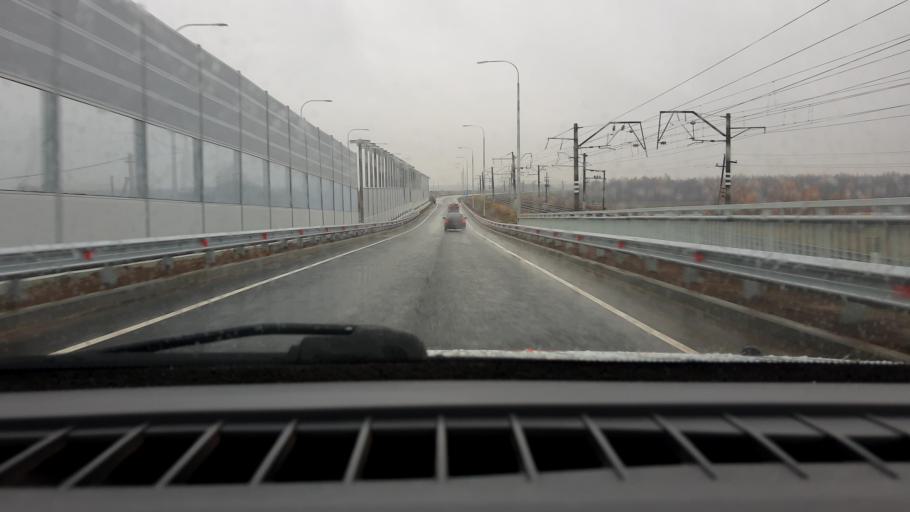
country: RU
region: Nizjnij Novgorod
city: Neklyudovo
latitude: 56.3984
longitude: 43.9816
